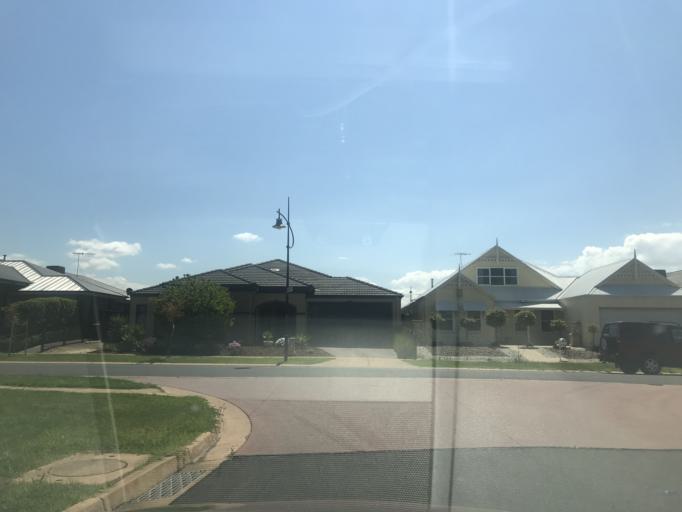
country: AU
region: Victoria
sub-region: Wyndham
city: Hoppers Crossing
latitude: -37.8850
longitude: 144.7262
